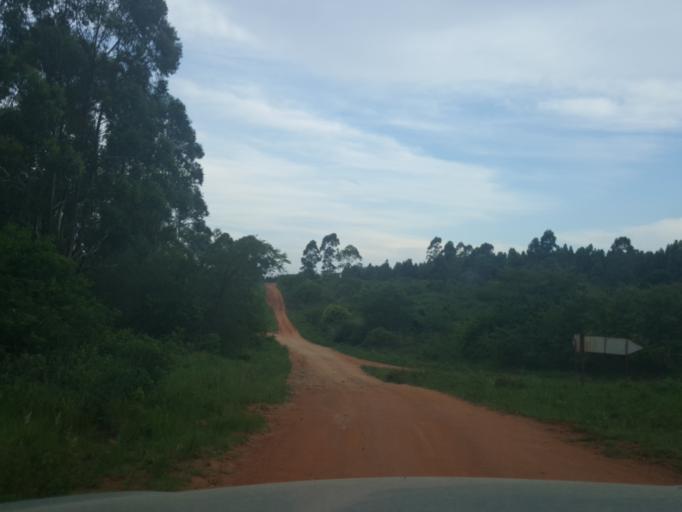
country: ZA
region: Limpopo
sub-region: Mopani District Municipality
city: Hoedspruit
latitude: -24.5978
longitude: 30.9231
